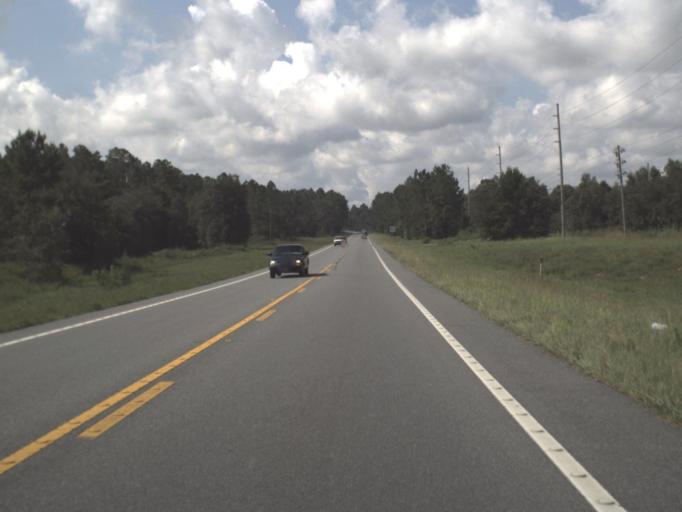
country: US
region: Florida
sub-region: Marion County
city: Dunnellon
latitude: 29.0252
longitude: -82.4562
